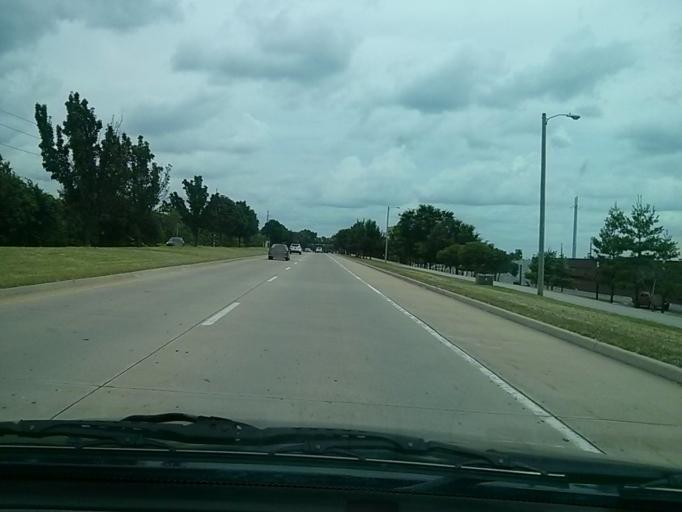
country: US
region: Oklahoma
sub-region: Tulsa County
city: Jenks
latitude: 36.0411
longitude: -95.9612
